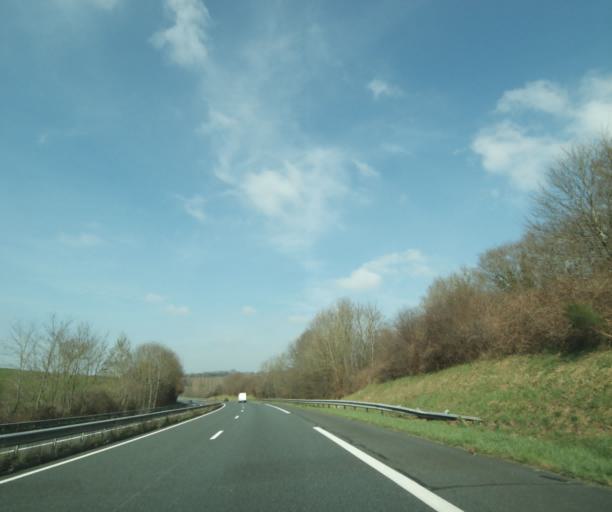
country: FR
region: Centre
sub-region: Departement de l'Indre
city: Chantome
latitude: 46.4598
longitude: 1.4992
